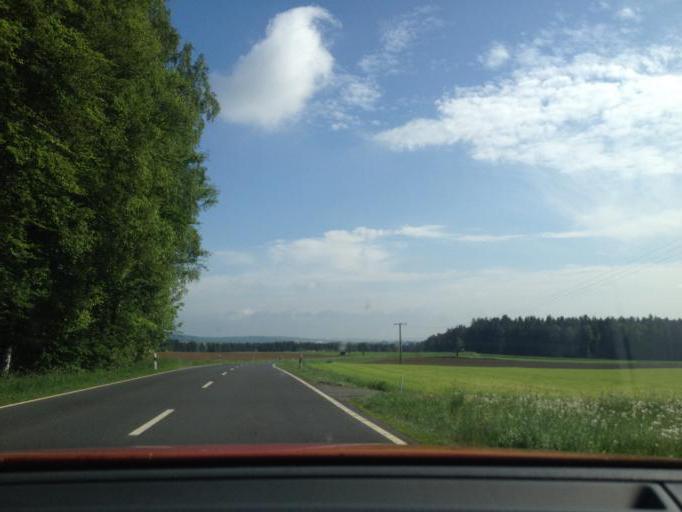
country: DE
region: Bavaria
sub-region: Upper Palatinate
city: Pullenreuth
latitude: 49.9557
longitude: 12.0299
